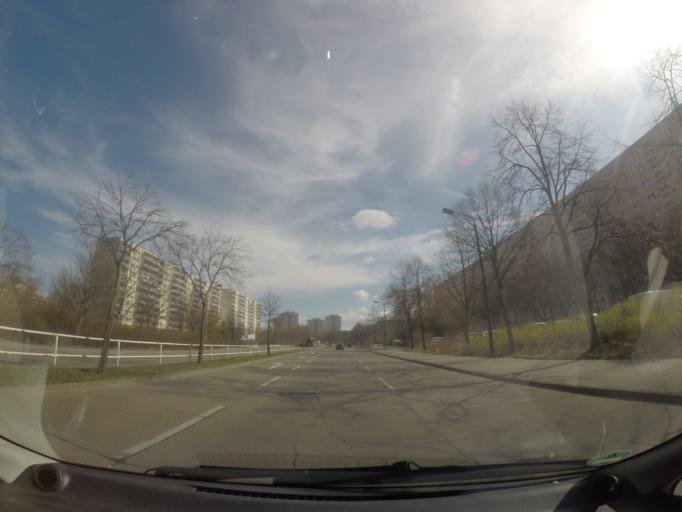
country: DE
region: Berlin
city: Falkenberg
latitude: 52.5574
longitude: 13.5558
